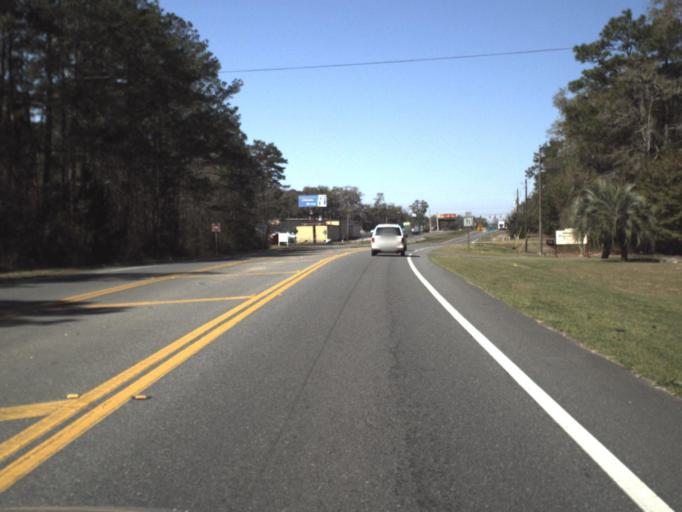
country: US
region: Florida
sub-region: Jackson County
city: Marianna
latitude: 30.7476
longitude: -85.1833
